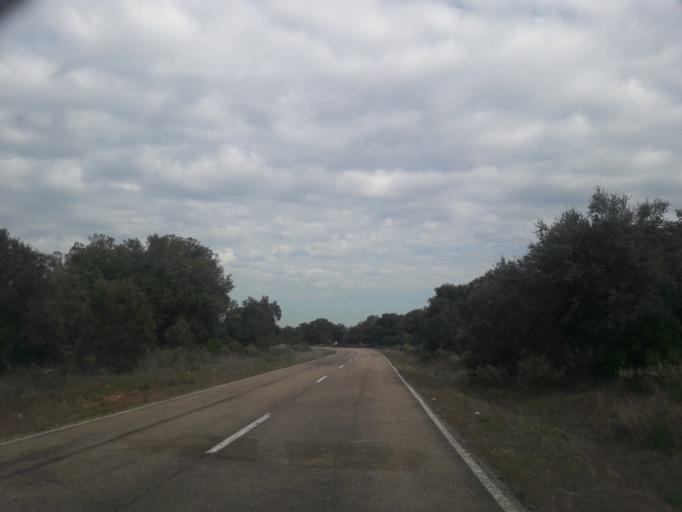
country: ES
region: Castille and Leon
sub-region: Provincia de Salamanca
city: Ciudad Rodrigo
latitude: 40.5726
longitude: -6.5306
